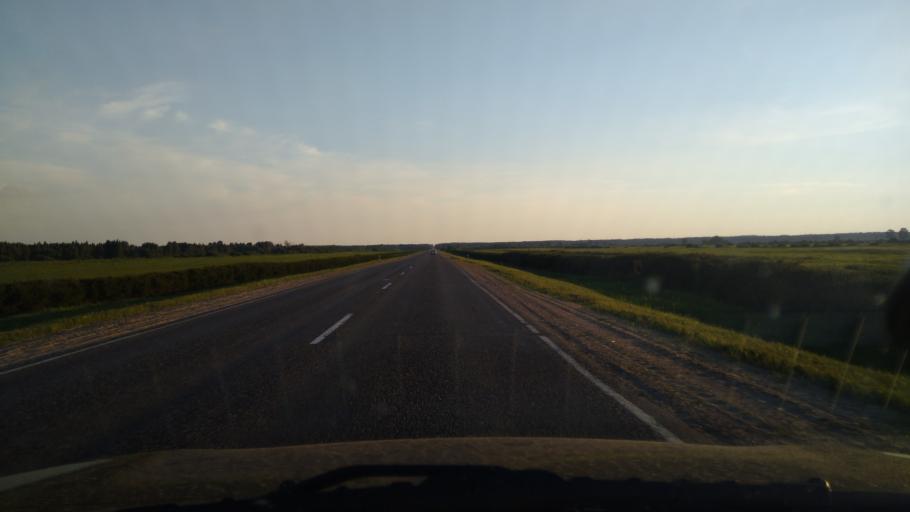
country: BY
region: Brest
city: Nyakhachava
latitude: 52.6317
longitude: 25.1802
